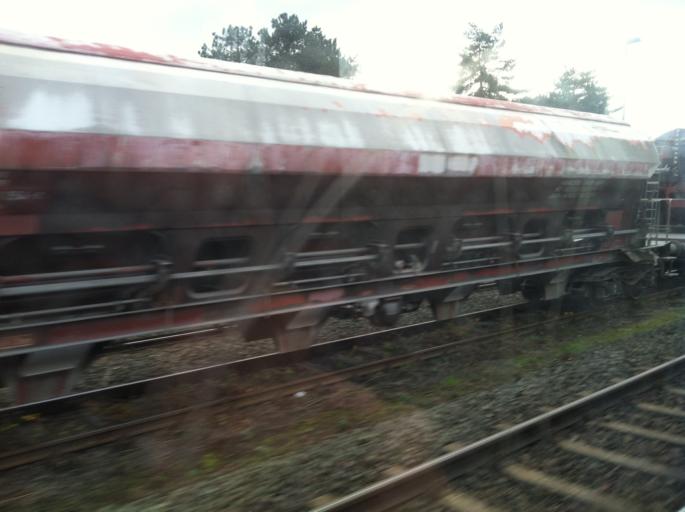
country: DE
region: North Rhine-Westphalia
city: Wesseling
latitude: 50.8540
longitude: 6.9901
